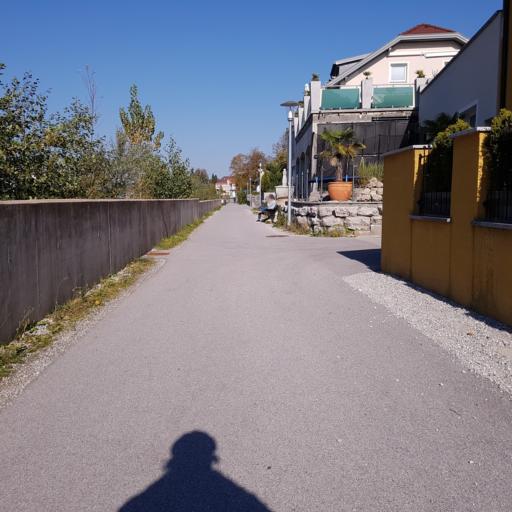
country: AT
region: Salzburg
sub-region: Politischer Bezirk Hallein
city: Hallein
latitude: 47.6795
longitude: 13.0992
